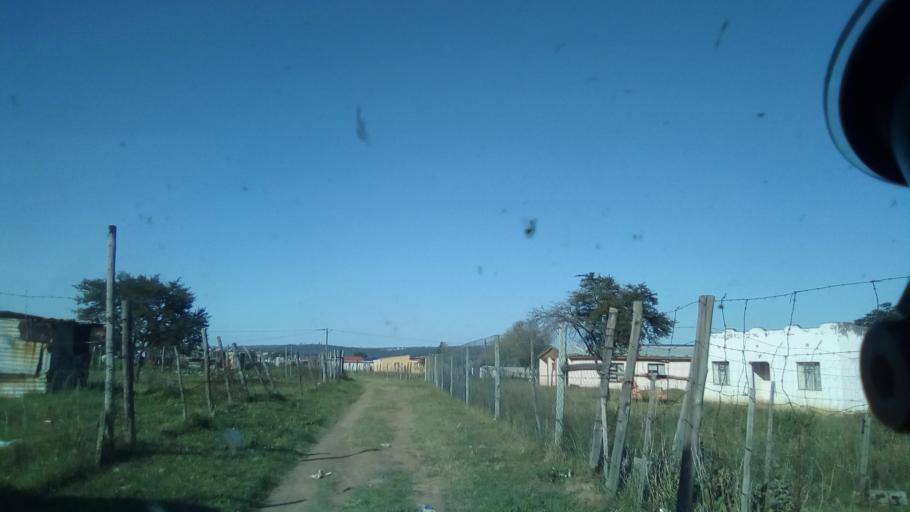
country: ZA
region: Eastern Cape
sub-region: Buffalo City Metropolitan Municipality
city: Bhisho
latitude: -32.8267
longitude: 27.3713
